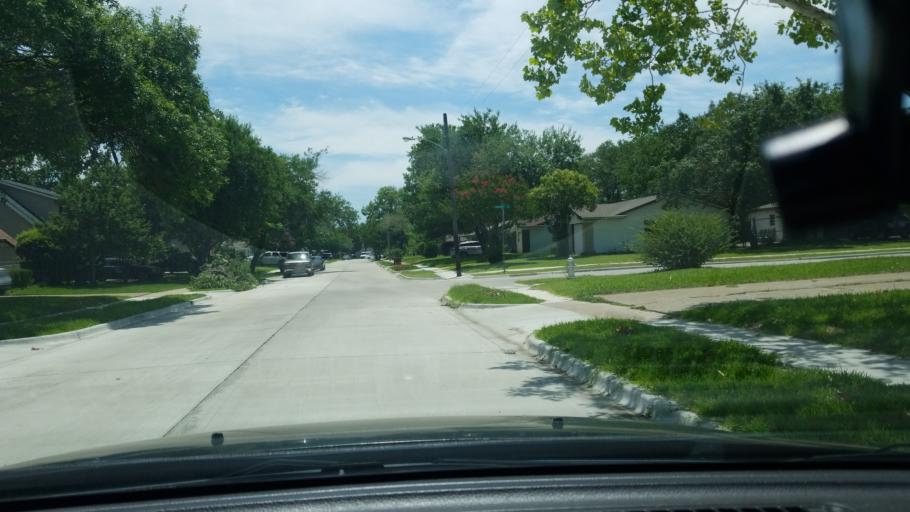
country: US
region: Texas
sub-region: Dallas County
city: Mesquite
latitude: 32.8044
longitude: -96.6511
